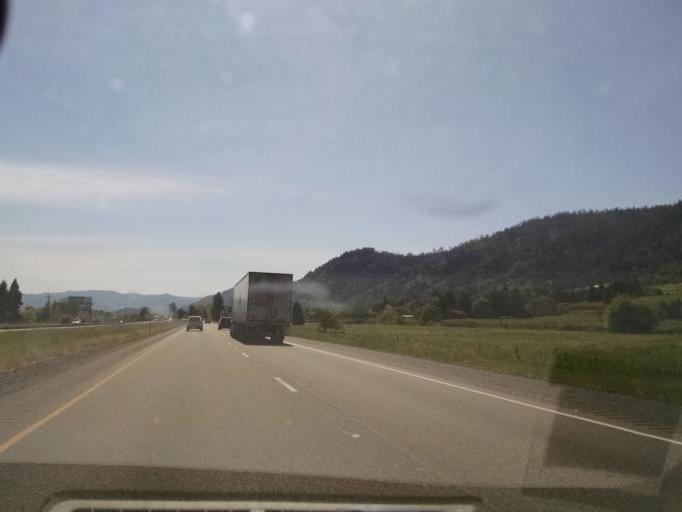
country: US
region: Oregon
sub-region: Douglas County
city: Tri-City
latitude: 43.0004
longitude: -123.3165
